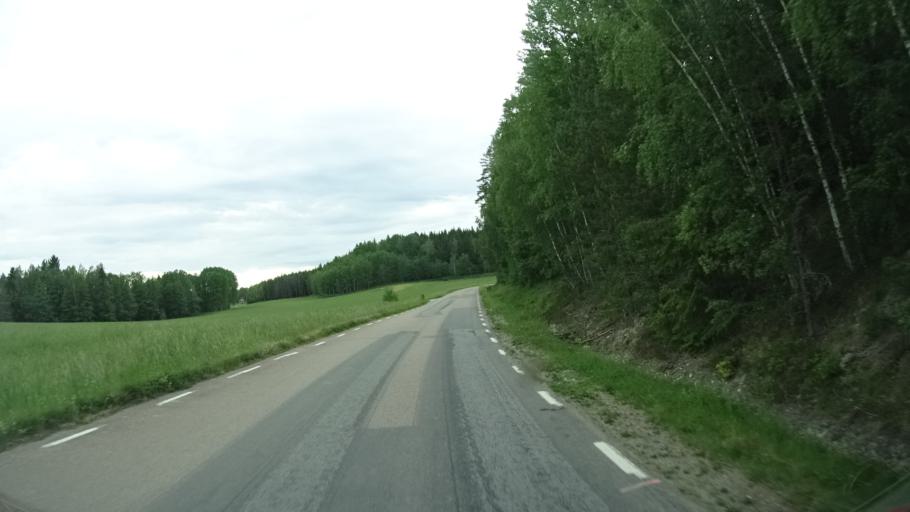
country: SE
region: Soedermanland
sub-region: Nykopings Kommun
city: Stigtomta
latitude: 58.7601
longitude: 16.7080
